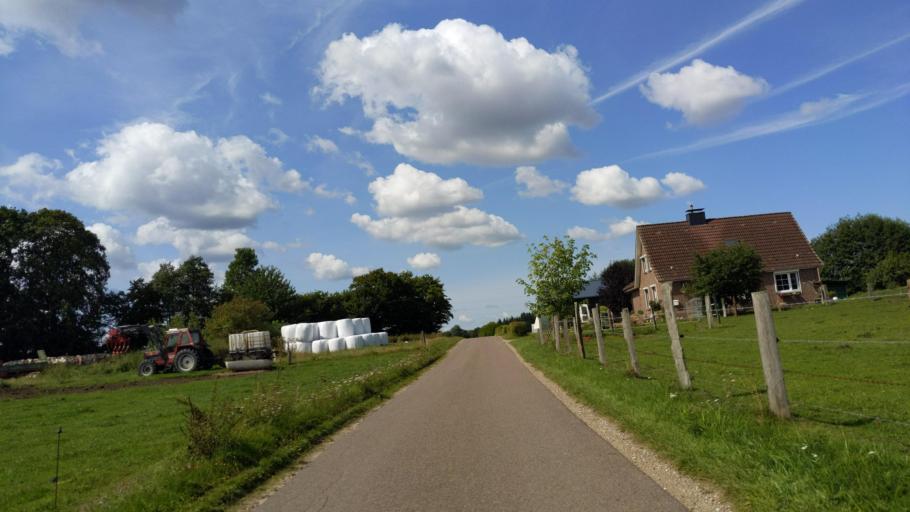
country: DE
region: Schleswig-Holstein
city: Altenkrempe
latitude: 54.1475
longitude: 10.8044
